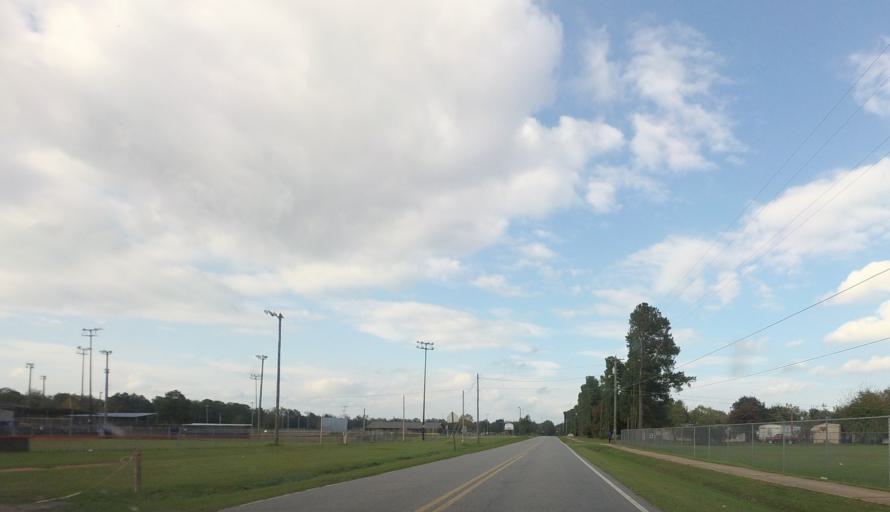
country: US
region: Georgia
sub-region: Houston County
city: Centerville
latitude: 32.6378
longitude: -83.6455
